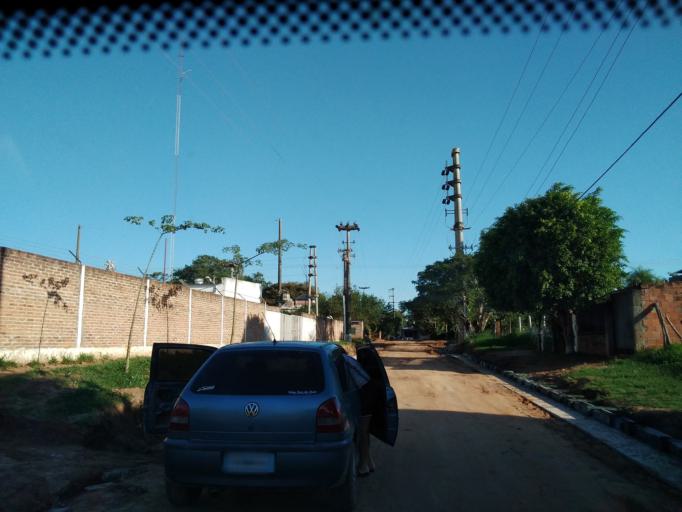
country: AR
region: Corrientes
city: Corrientes
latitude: -27.5054
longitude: -58.7943
